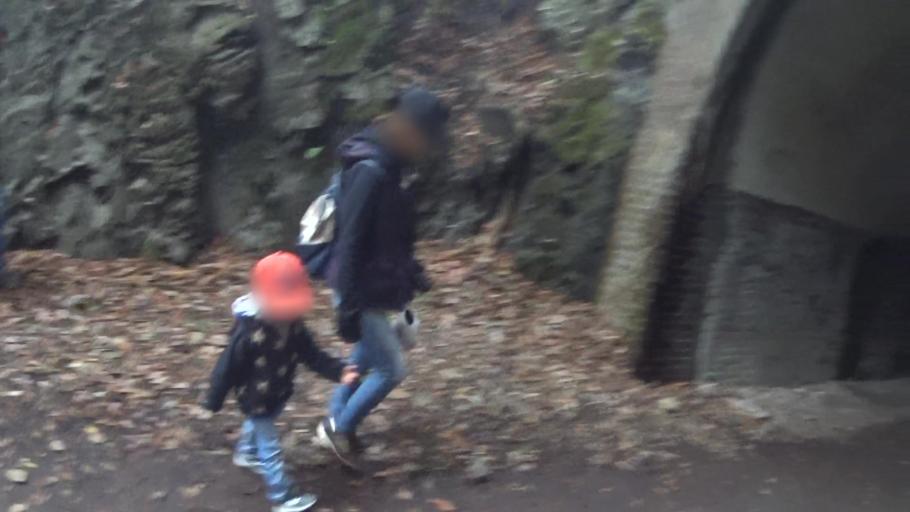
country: JP
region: Hyogo
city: Takarazuka
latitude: 34.8547
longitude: 135.3163
